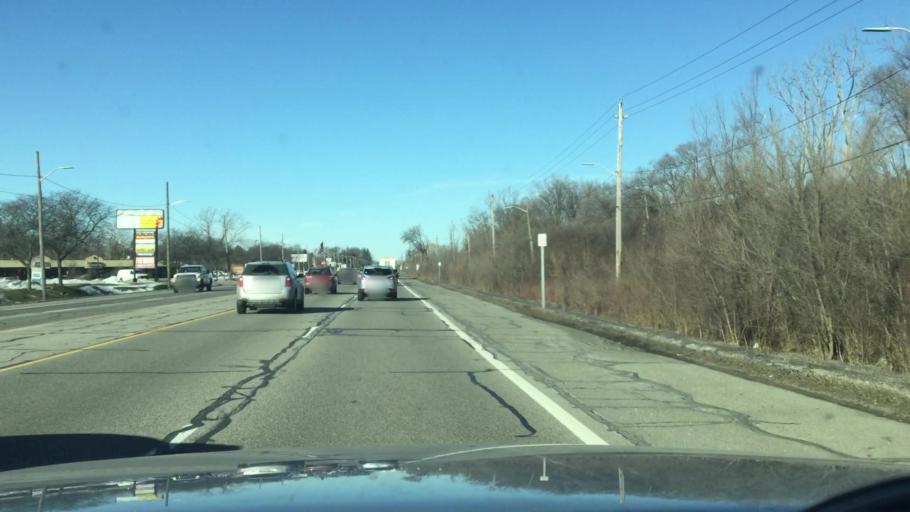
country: US
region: Michigan
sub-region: Oakland County
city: Keego Harbor
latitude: 42.6434
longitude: -83.3577
